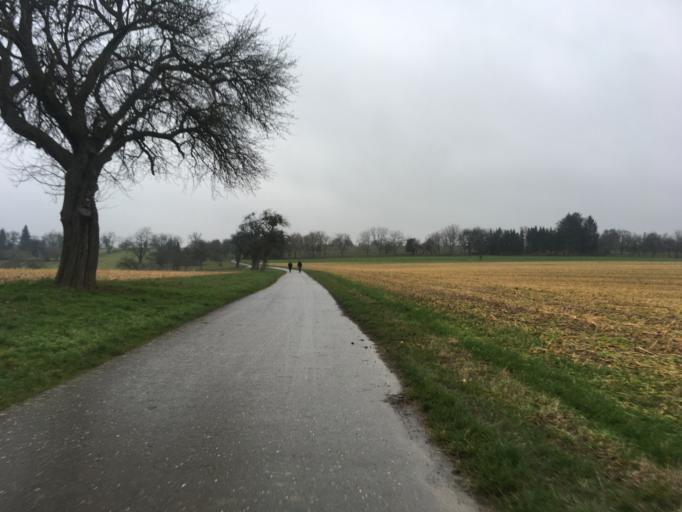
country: DE
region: Baden-Wuerttemberg
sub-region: Karlsruhe Region
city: Ettlingen
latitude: 48.9691
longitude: 8.4898
